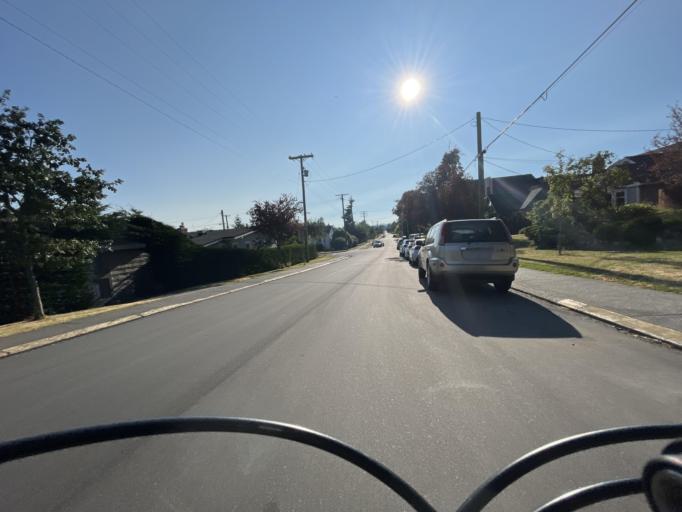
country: CA
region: British Columbia
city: Oak Bay
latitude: 48.4358
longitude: -123.3188
